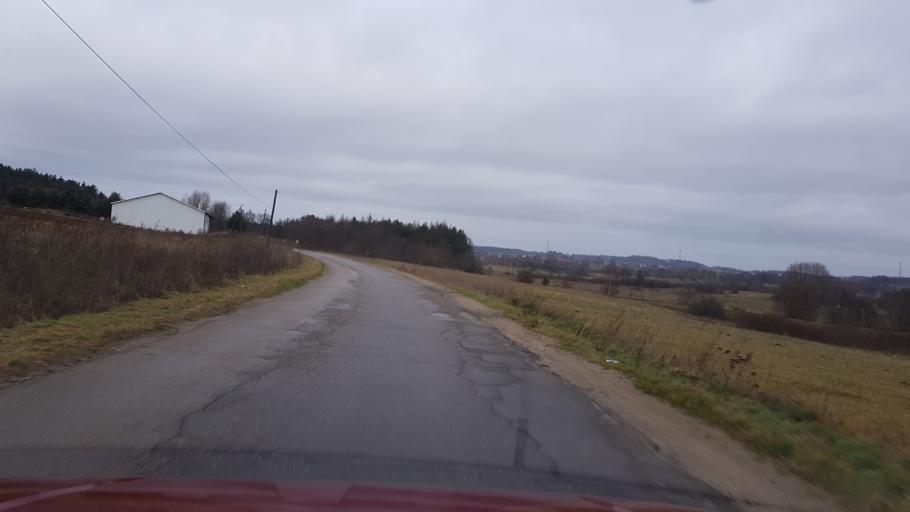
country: PL
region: Pomeranian Voivodeship
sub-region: Powiat bytowski
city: Borzytuchom
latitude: 54.1832
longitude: 17.3647
